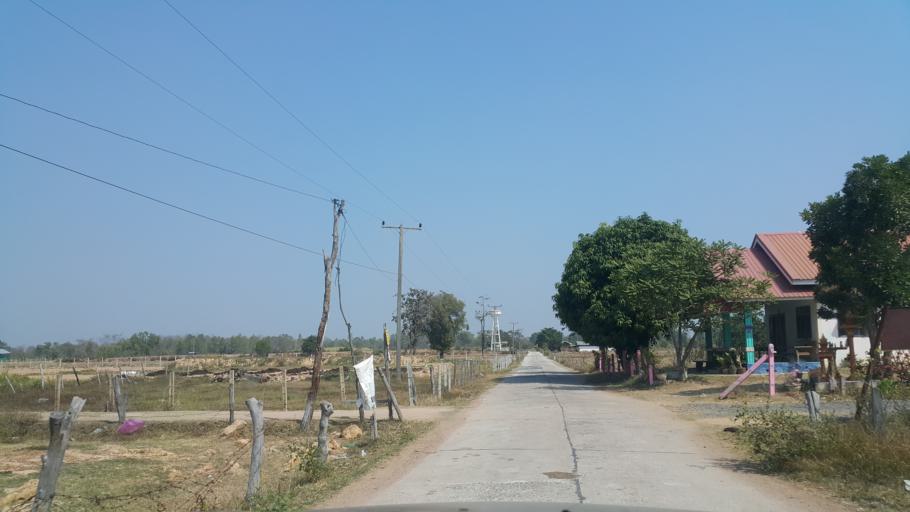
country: TH
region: Buriram
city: Krasang
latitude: 15.0983
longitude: 103.3725
